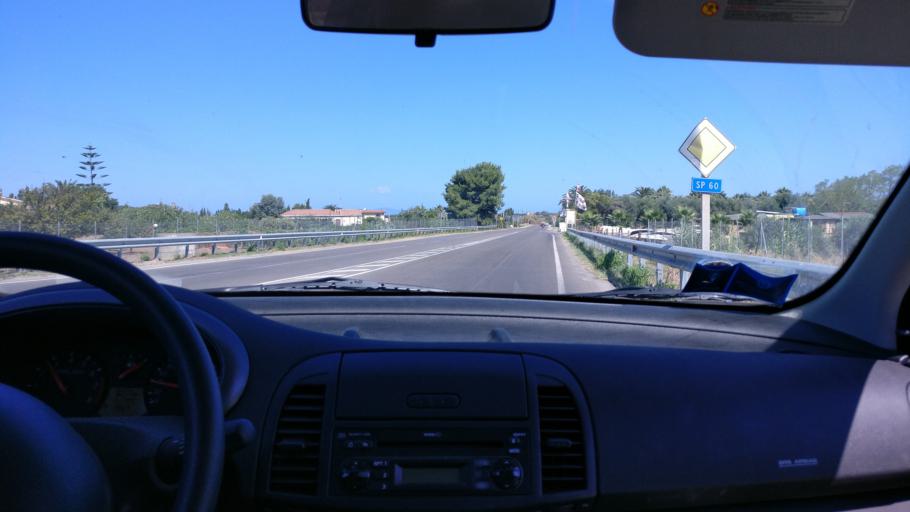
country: IT
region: Sardinia
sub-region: Provincia di Sassari
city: Ottava
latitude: 40.8013
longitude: 8.5084
